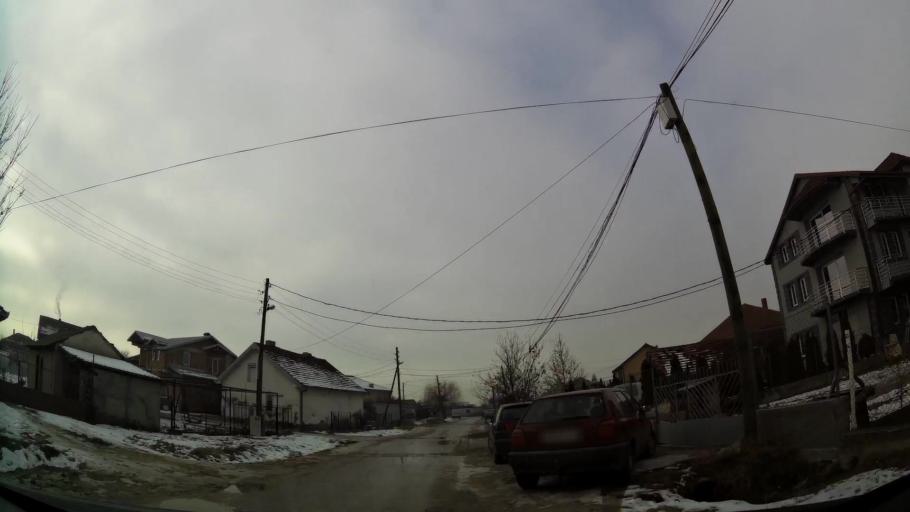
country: MK
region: Ilinden
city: Ilinden
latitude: 41.9920
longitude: 21.5745
